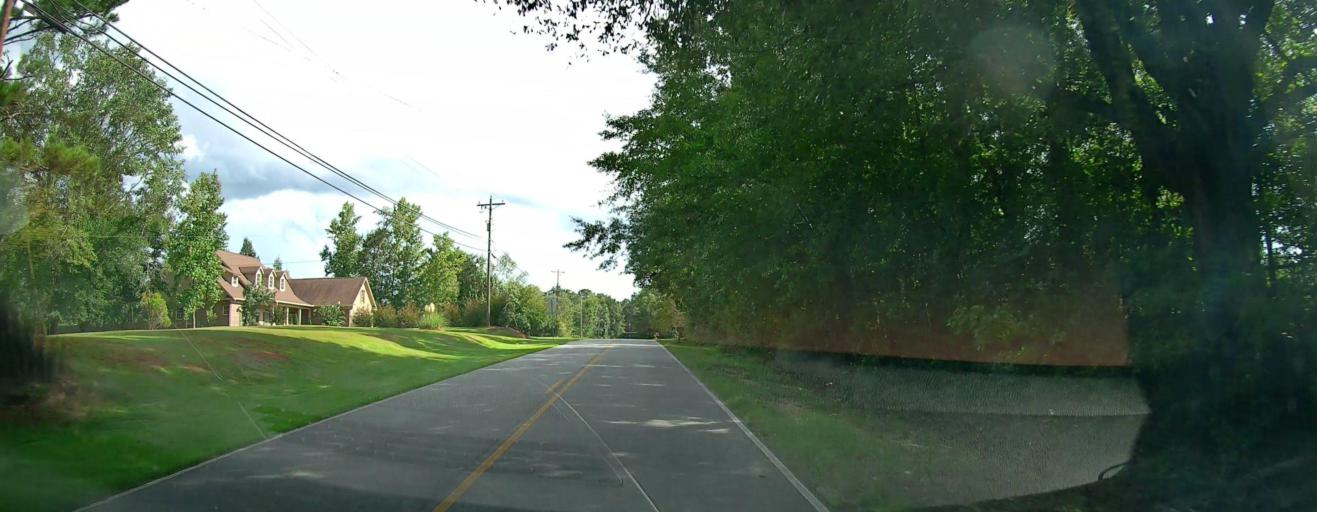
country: US
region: Alabama
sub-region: Russell County
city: Phenix City
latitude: 32.5900
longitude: -84.9782
